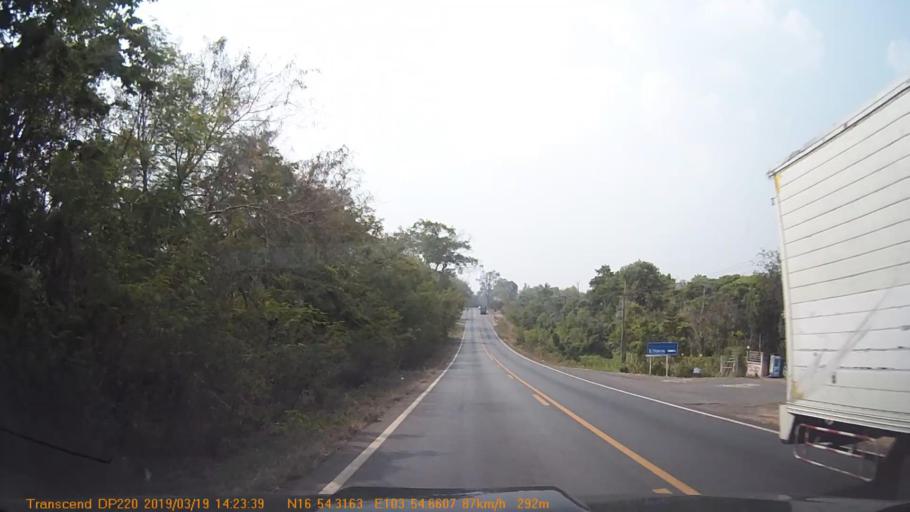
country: TH
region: Sakon Nakhon
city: Phu Phan
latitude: 16.9058
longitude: 103.9106
